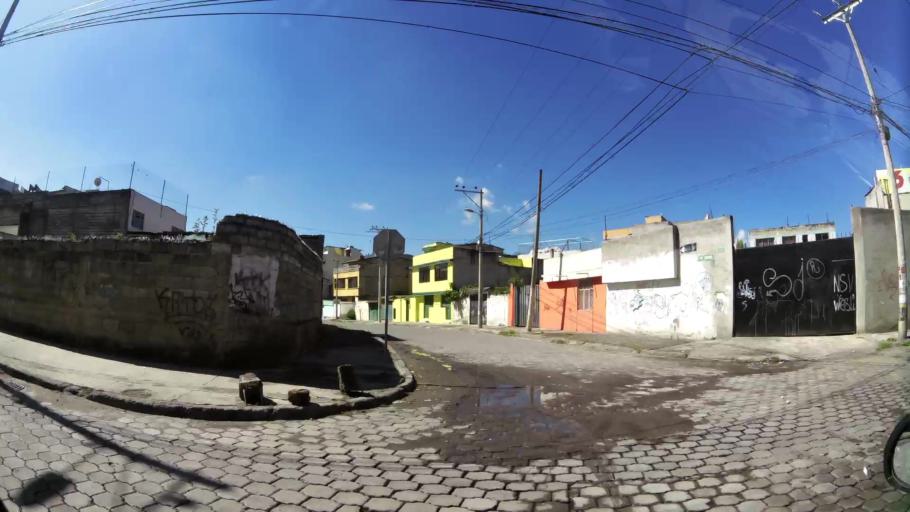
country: EC
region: Pichincha
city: Quito
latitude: -0.2455
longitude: -78.5289
